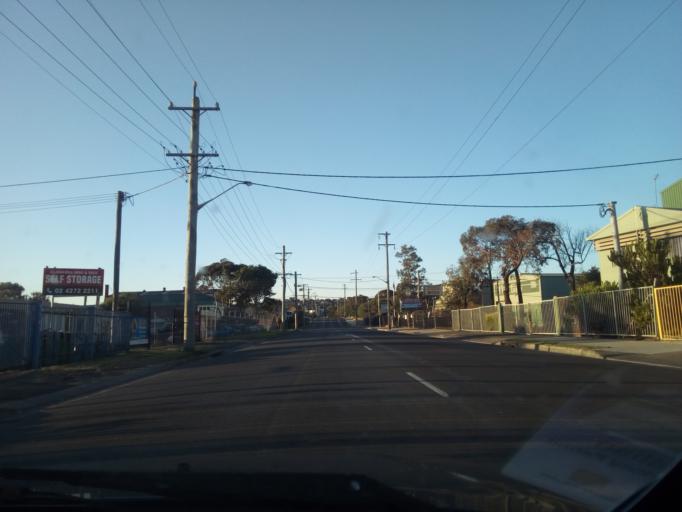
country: AU
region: New South Wales
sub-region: Wollongong
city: Port Kembla
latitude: -34.4939
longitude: 150.8925
